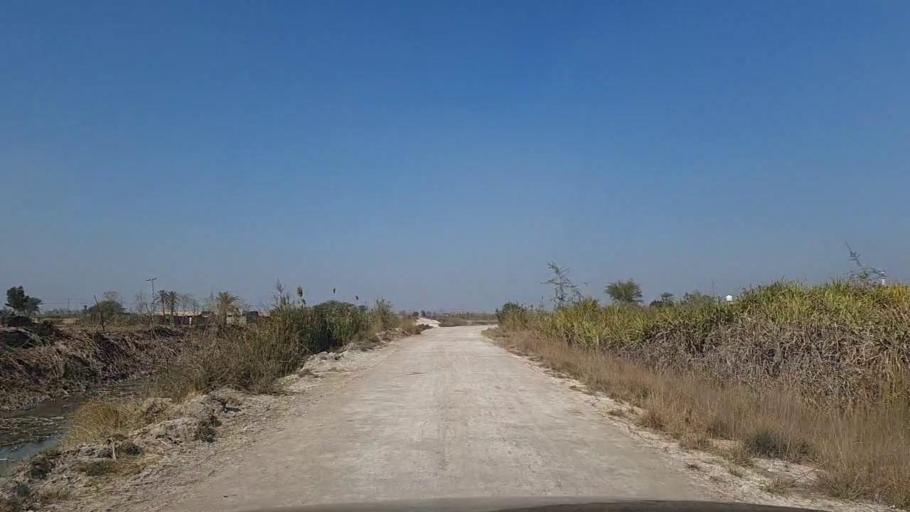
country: PK
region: Sindh
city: Bandhi
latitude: 26.5233
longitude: 68.3112
